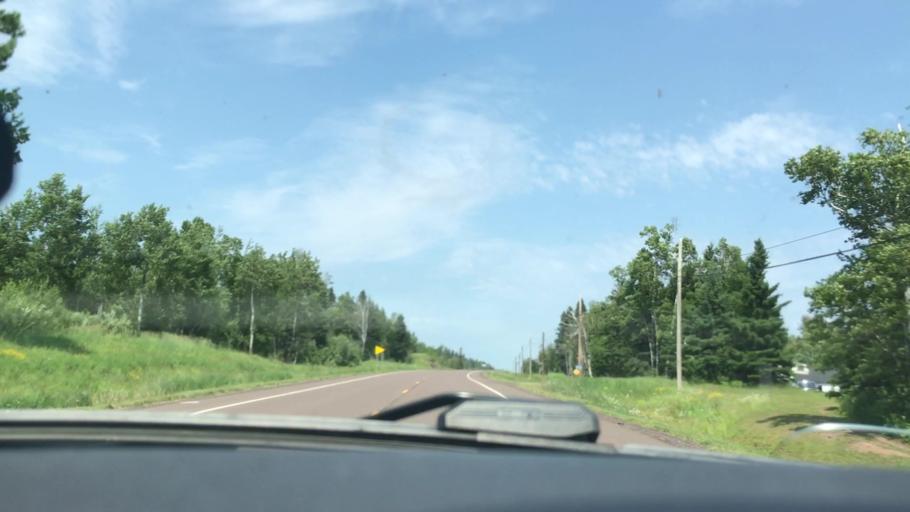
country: US
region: Minnesota
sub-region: Lake County
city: Silver Bay
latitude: 47.4285
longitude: -91.0889
